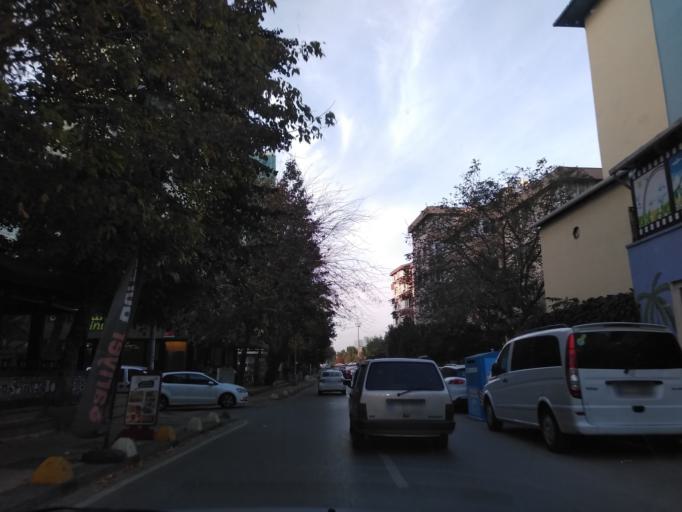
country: TR
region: Istanbul
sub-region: Atasehir
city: Atasehir
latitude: 40.9793
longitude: 29.0923
